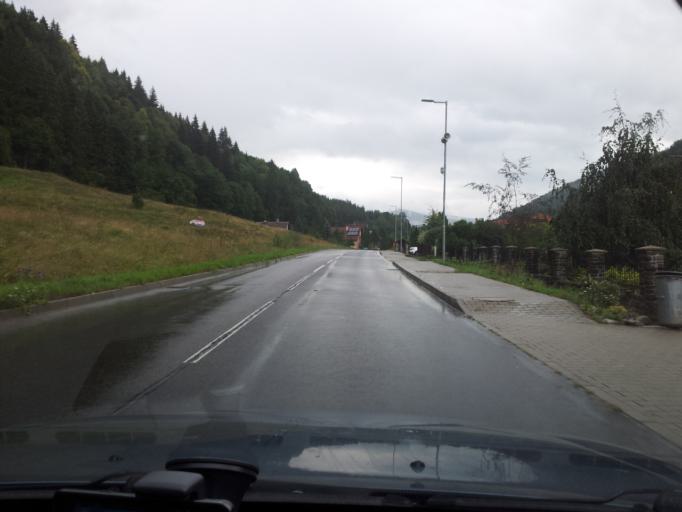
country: SK
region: Banskobystricky
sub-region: Okres Banska Bystrica
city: Brezno
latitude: 48.8401
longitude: 19.5904
